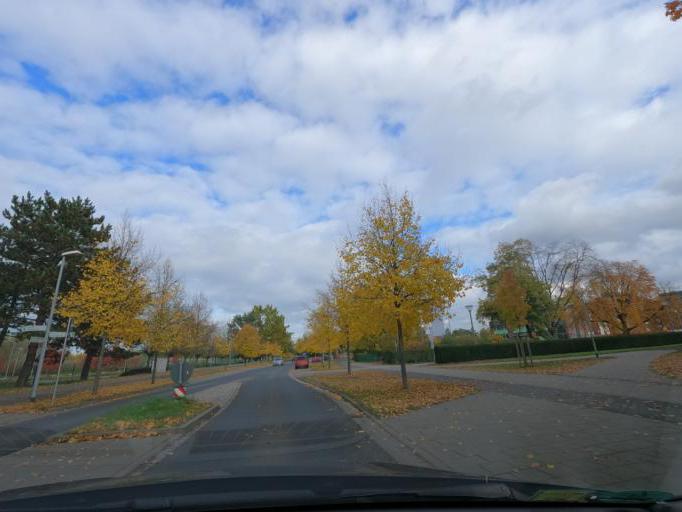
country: DE
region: Lower Saxony
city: Leiferde
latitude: 52.2327
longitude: 10.5234
